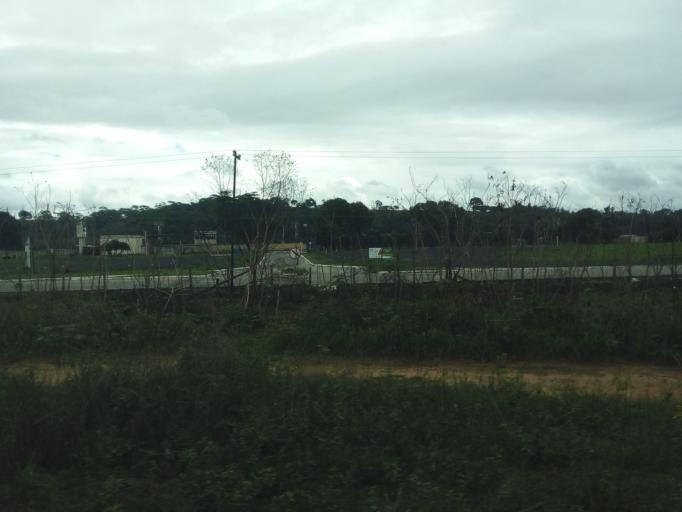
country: BR
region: Minas Gerais
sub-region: Ipatinga
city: Ipatinga
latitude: -19.4759
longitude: -42.4863
